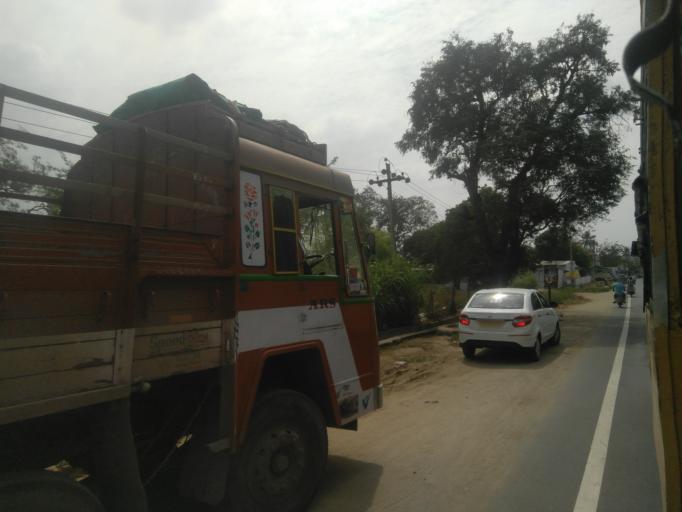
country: IN
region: Tamil Nadu
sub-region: Coimbatore
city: Irugur
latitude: 11.0091
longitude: 77.0780
